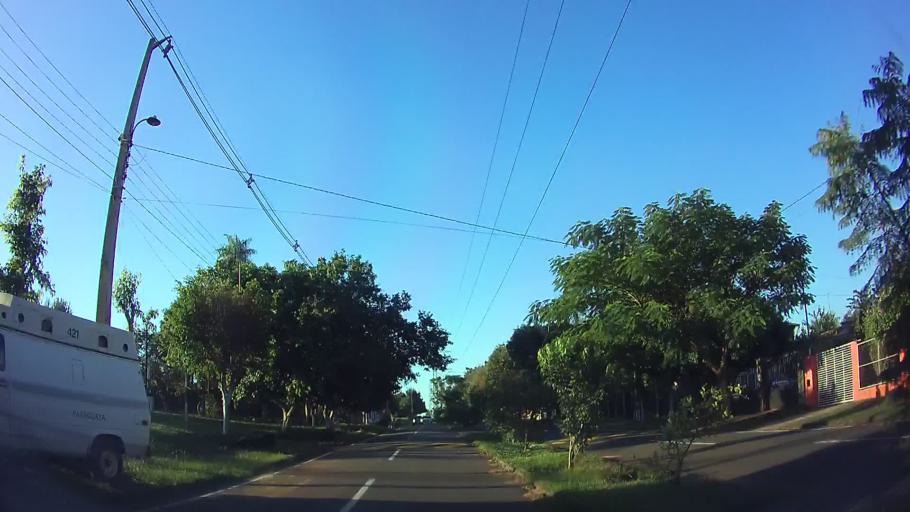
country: PY
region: Central
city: San Lorenzo
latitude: -25.2791
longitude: -57.4646
